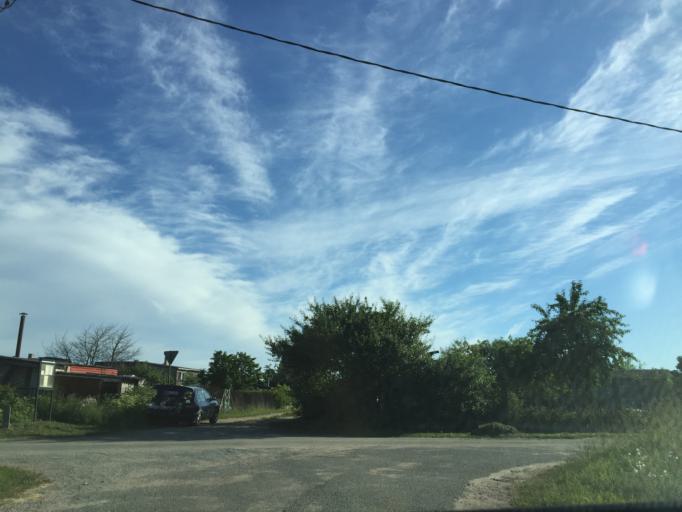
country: LV
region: Ventspils
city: Ventspils
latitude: 57.3669
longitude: 21.6005
